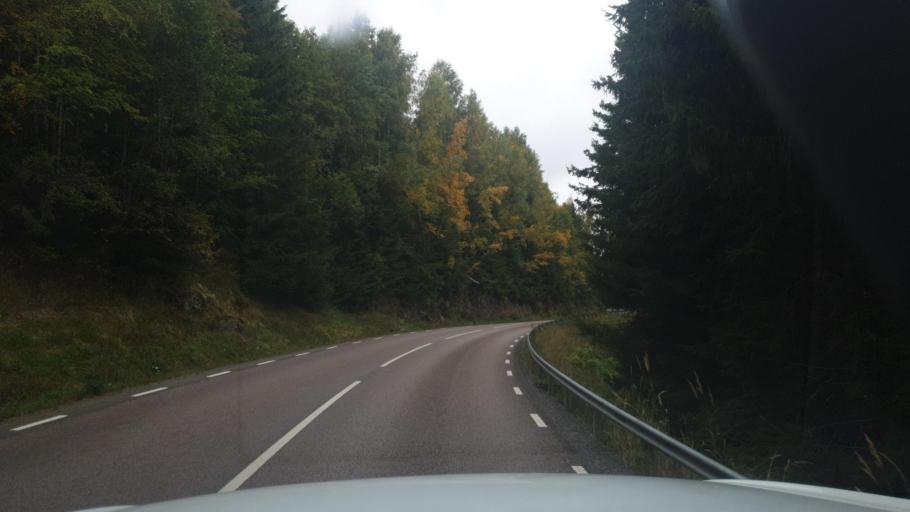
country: SE
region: Vaermland
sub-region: Sunne Kommun
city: Sunne
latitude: 59.8263
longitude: 12.9877
